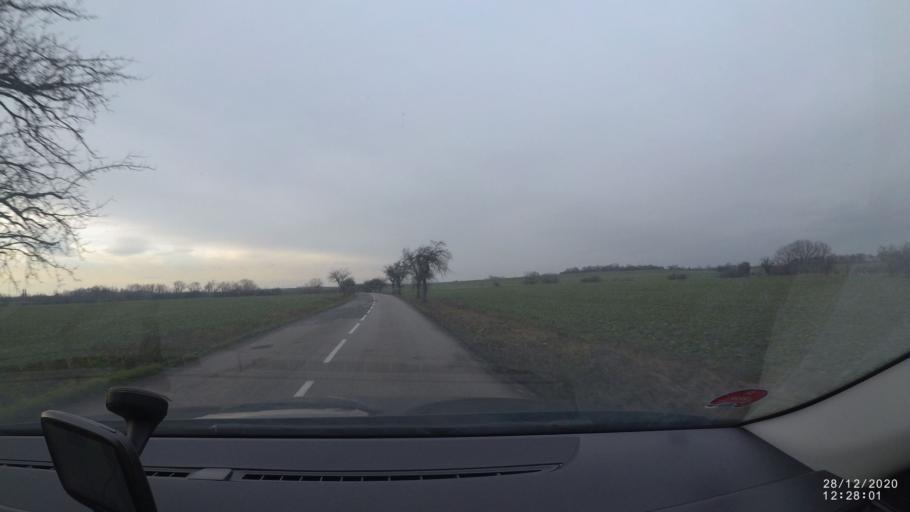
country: CZ
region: Central Bohemia
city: Brandys nad Labem-Stara Boleslav
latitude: 50.1947
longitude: 14.6392
